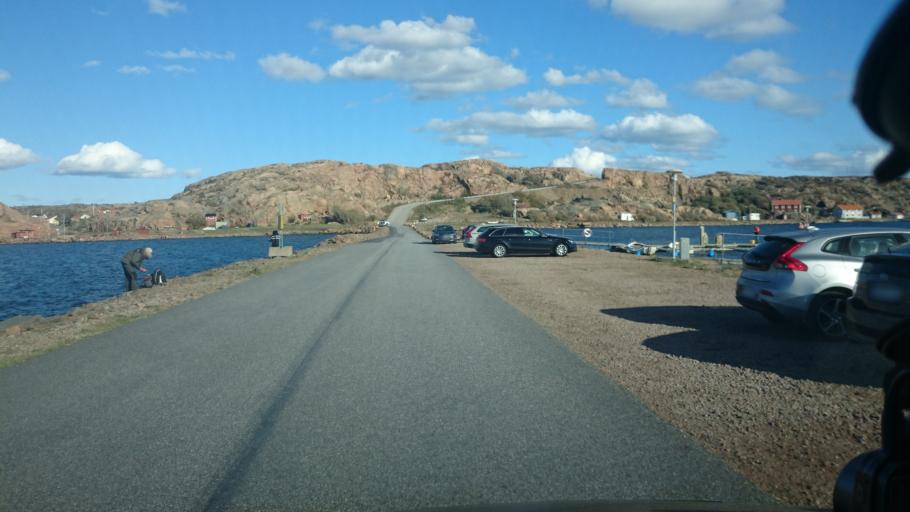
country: SE
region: Vaestra Goetaland
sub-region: Lysekils Kommun
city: Lysekil
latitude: 58.3173
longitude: 11.3970
